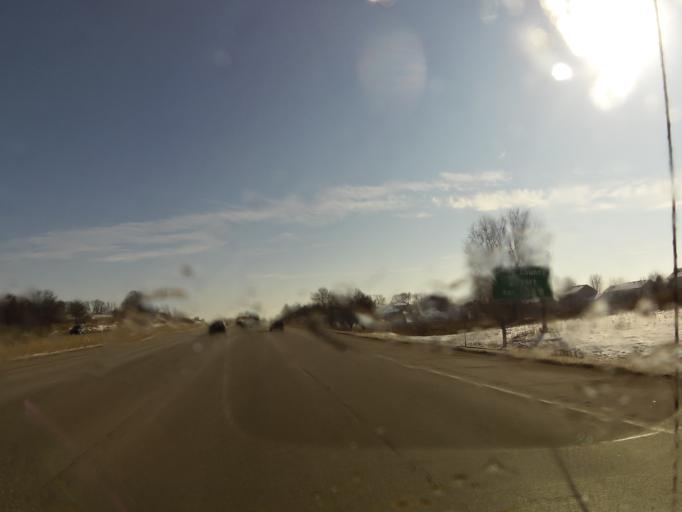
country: US
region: Wisconsin
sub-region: Dane County
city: Monona
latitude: 43.1180
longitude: -89.2882
